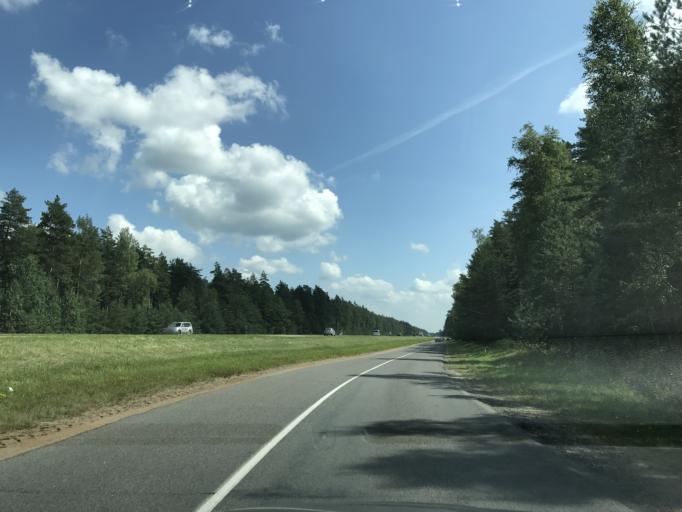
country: BY
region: Minsk
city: Rakaw
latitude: 53.9838
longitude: 26.9946
